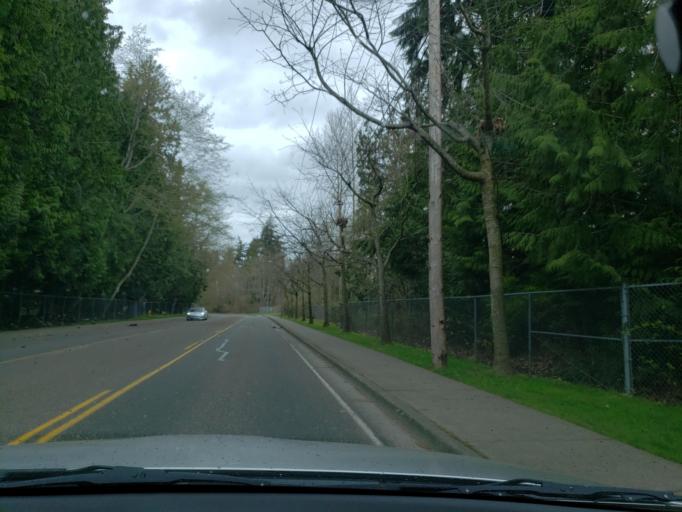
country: US
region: Washington
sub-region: Snohomish County
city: Mukilteo
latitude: 47.8959
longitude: -122.3009
